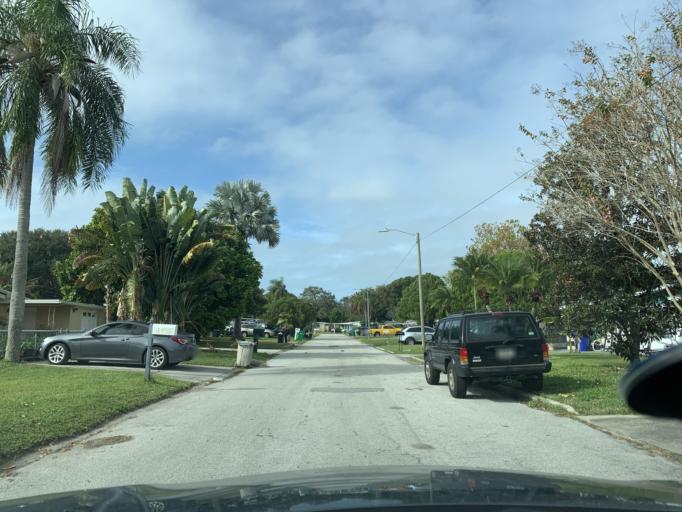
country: US
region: Florida
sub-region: Pinellas County
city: Ridgecrest
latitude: 27.8785
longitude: -82.7803
